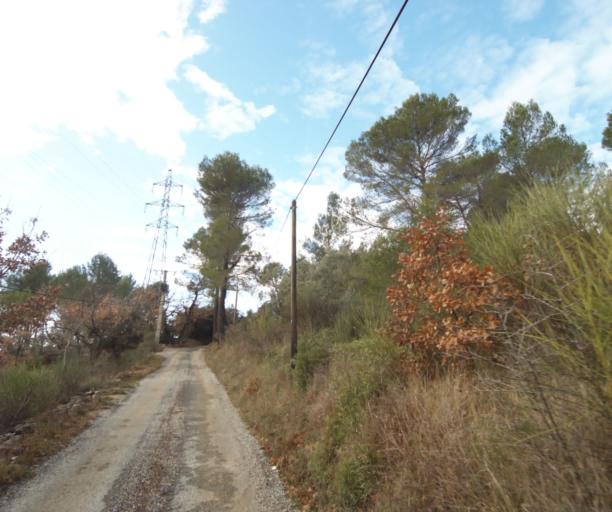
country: FR
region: Provence-Alpes-Cote d'Azur
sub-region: Departement du Var
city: Trans-en-Provence
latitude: 43.4993
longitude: 6.4670
